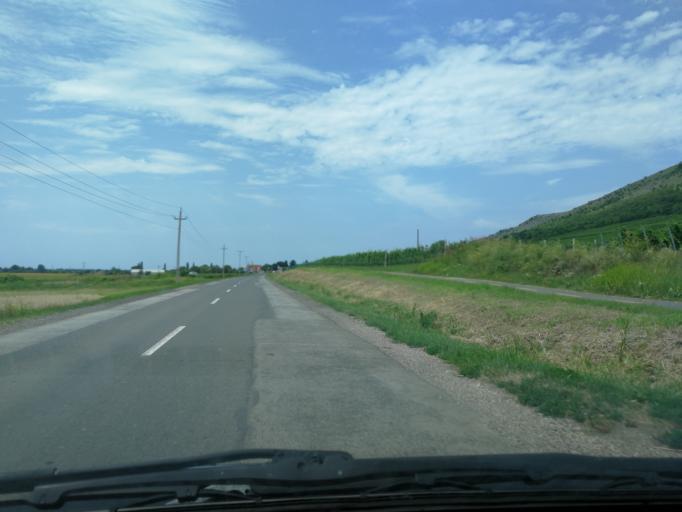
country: HU
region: Baranya
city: Villany
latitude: 45.8482
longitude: 18.4158
